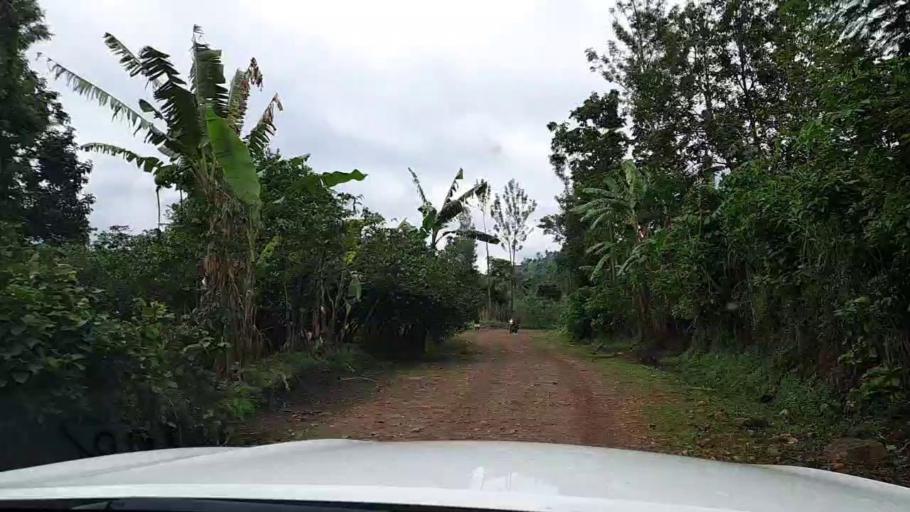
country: RW
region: Western Province
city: Cyangugu
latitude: -2.5520
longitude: 29.0371
